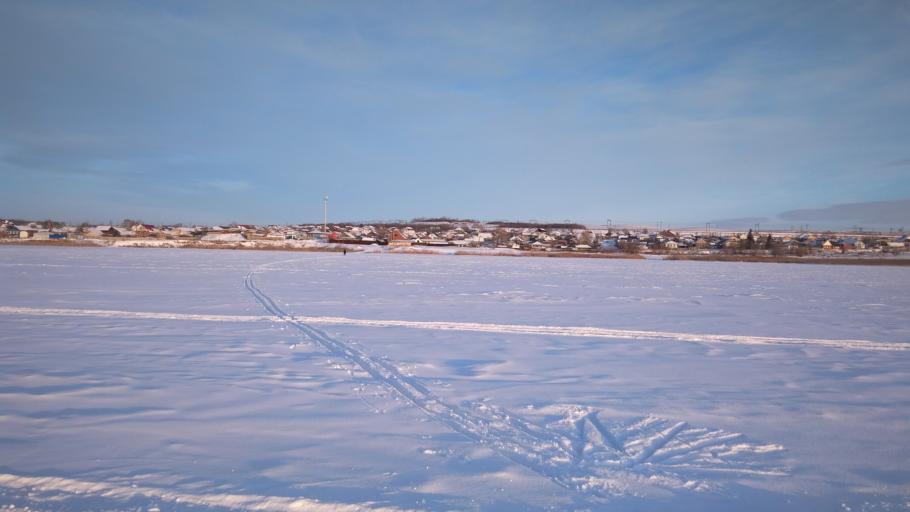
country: RU
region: Chelyabinsk
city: Troitsk
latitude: 54.0856
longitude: 61.5863
